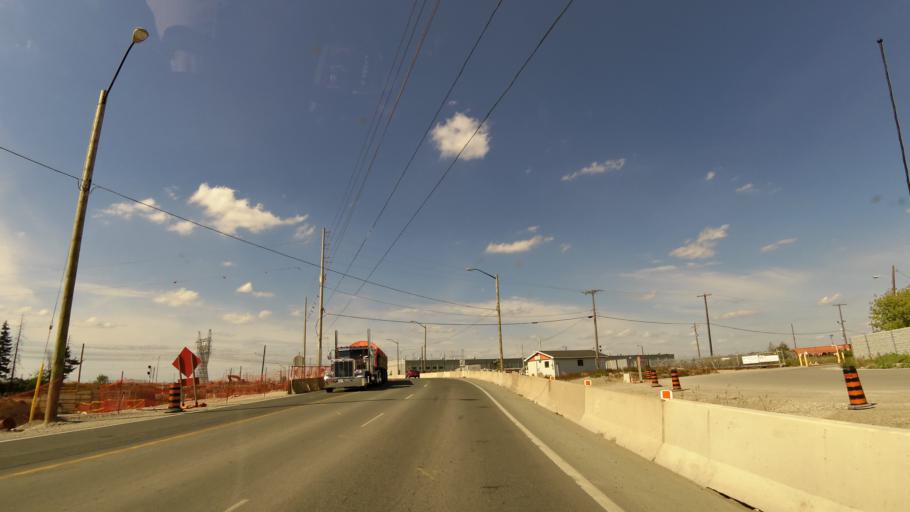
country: CA
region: Ontario
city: Brampton
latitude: 43.7075
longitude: -79.6702
